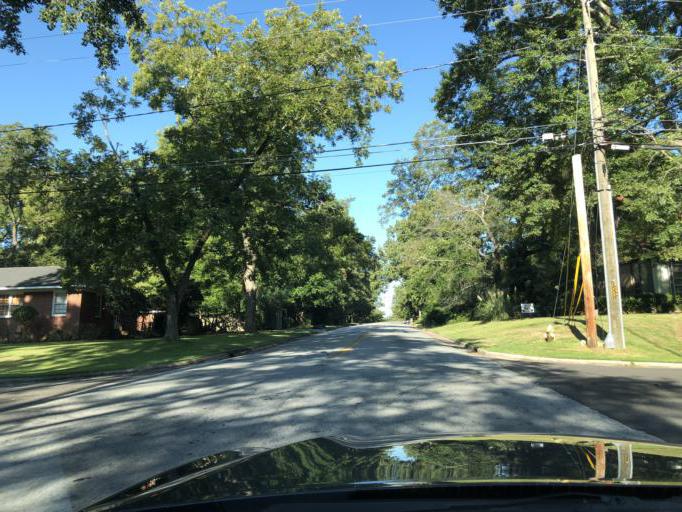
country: US
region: Georgia
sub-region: Muscogee County
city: Columbus
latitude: 32.4786
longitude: -84.9497
